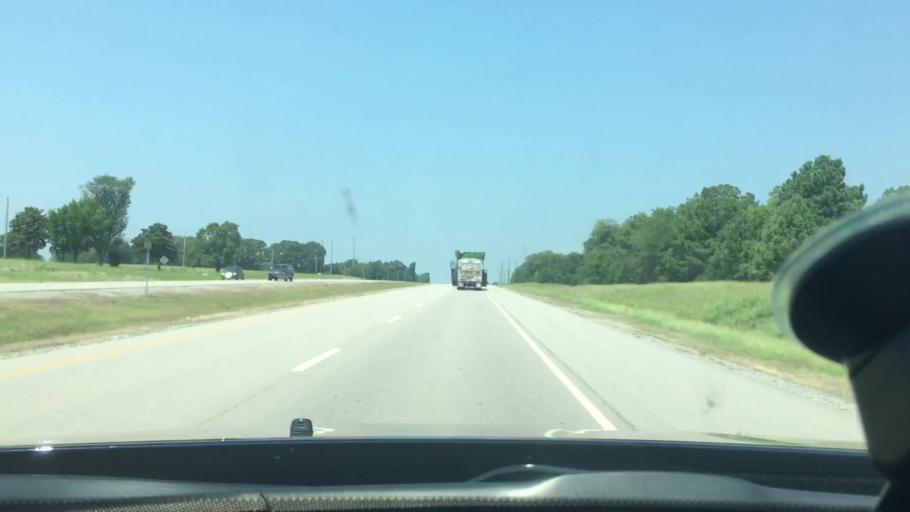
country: US
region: Oklahoma
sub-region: Atoka County
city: Atoka
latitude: 34.3262
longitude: -96.0439
